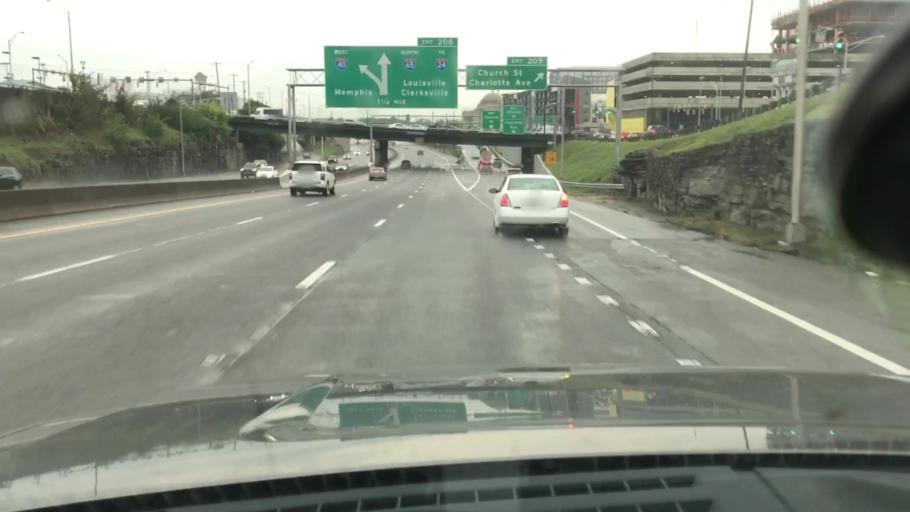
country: US
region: Tennessee
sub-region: Davidson County
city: Nashville
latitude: 36.1550
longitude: -86.7877
